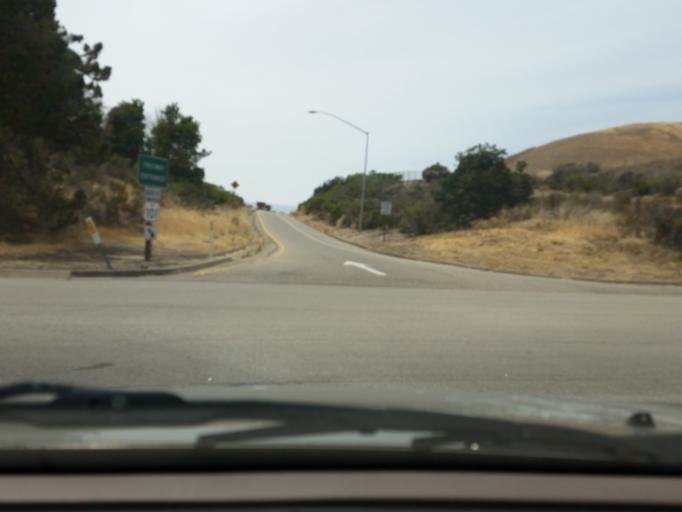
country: US
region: California
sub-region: San Luis Obispo County
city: Pismo Beach
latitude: 35.1513
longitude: -120.6545
